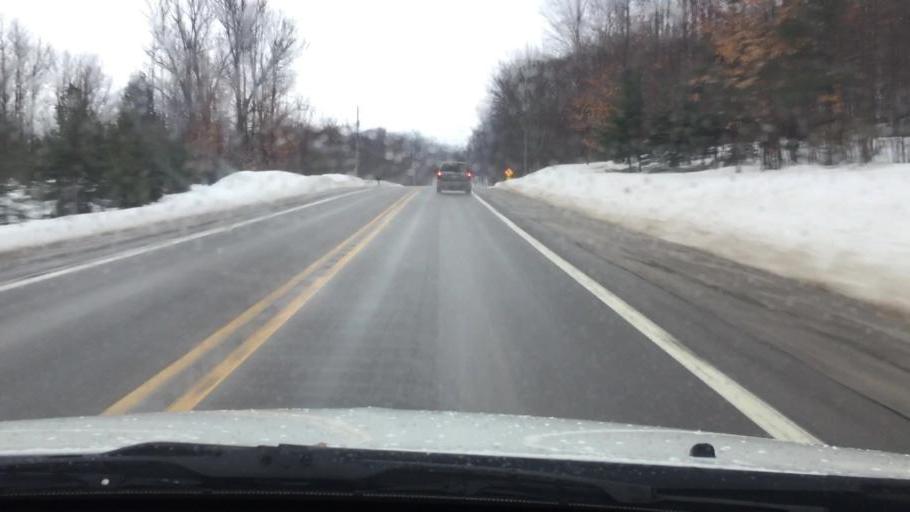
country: US
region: Michigan
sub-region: Charlevoix County
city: East Jordan
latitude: 45.2233
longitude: -85.1774
